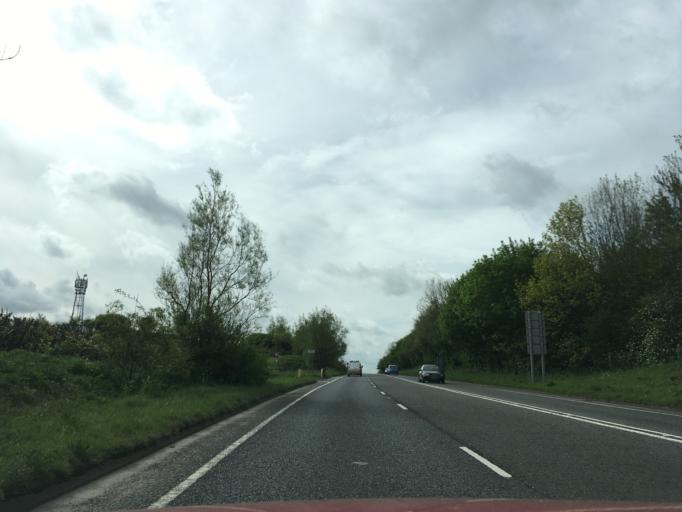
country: GB
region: England
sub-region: Bath and North East Somerset
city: Peasedown Saint John
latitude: 51.3216
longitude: -2.4154
